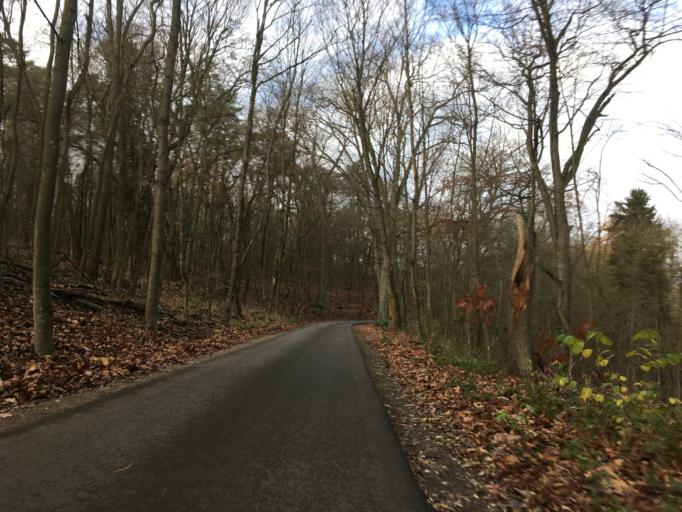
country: DE
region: Brandenburg
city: Buckow
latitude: 52.5681
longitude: 14.0930
